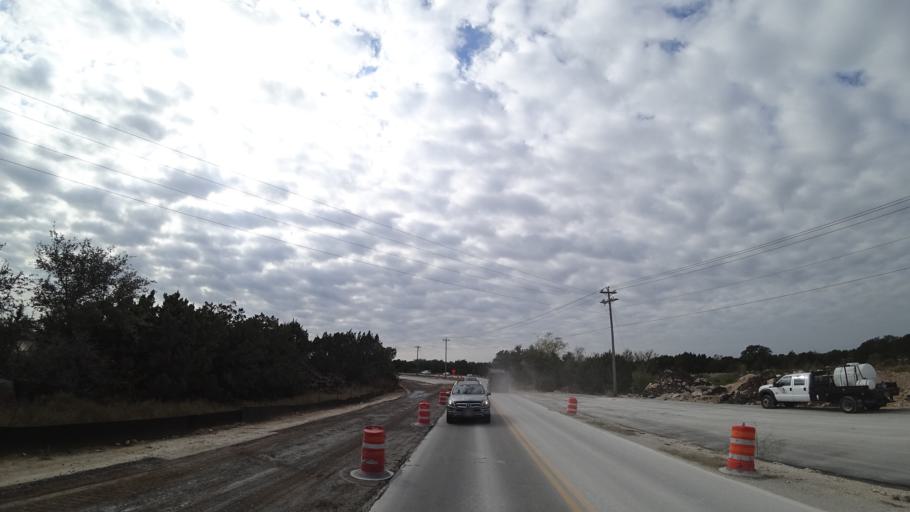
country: US
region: Texas
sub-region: Williamson County
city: Cedar Park
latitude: 30.5025
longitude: -97.8577
